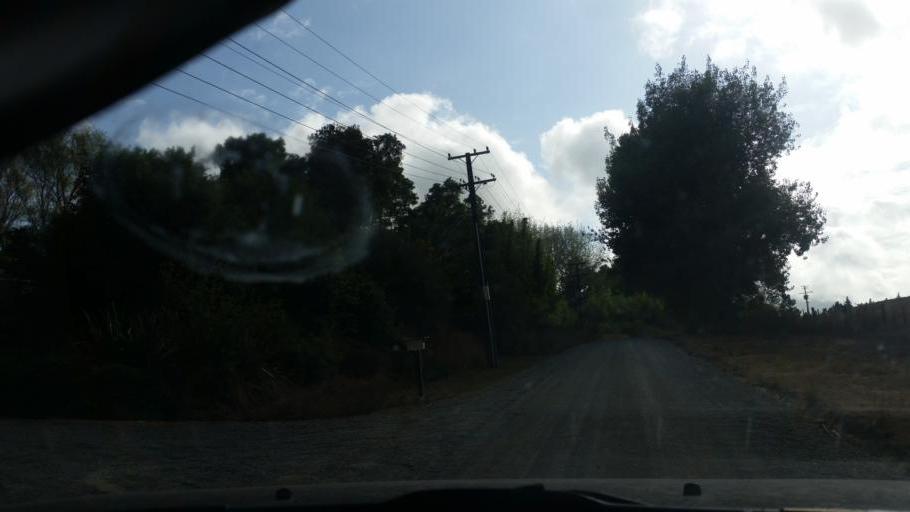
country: NZ
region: Auckland
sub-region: Auckland
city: Wellsford
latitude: -36.1651
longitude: 174.4466
